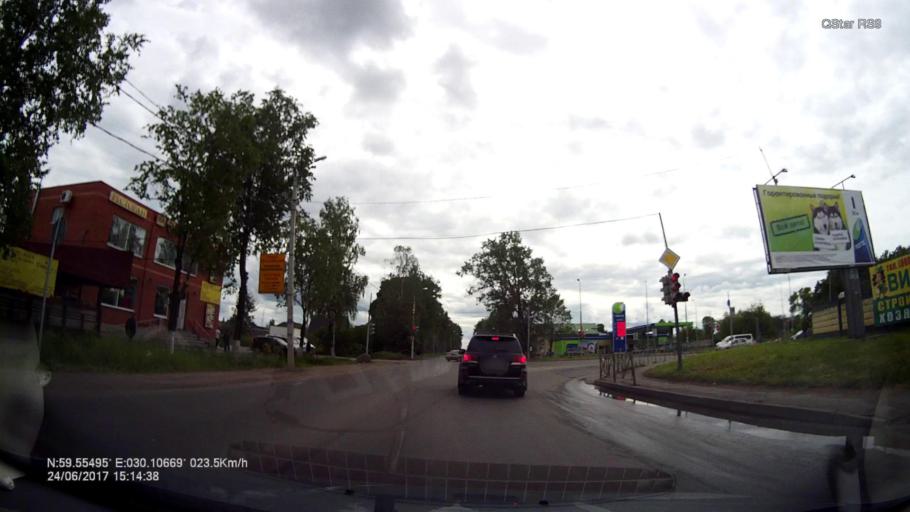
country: RU
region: Leningrad
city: Gatchina
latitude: 59.5549
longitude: 30.1066
